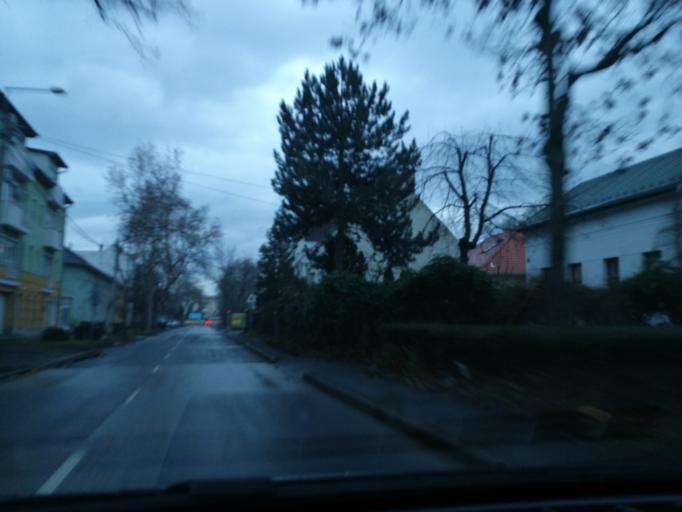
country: HU
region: Szabolcs-Szatmar-Bereg
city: Nyiregyhaza
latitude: 47.9440
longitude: 21.7153
